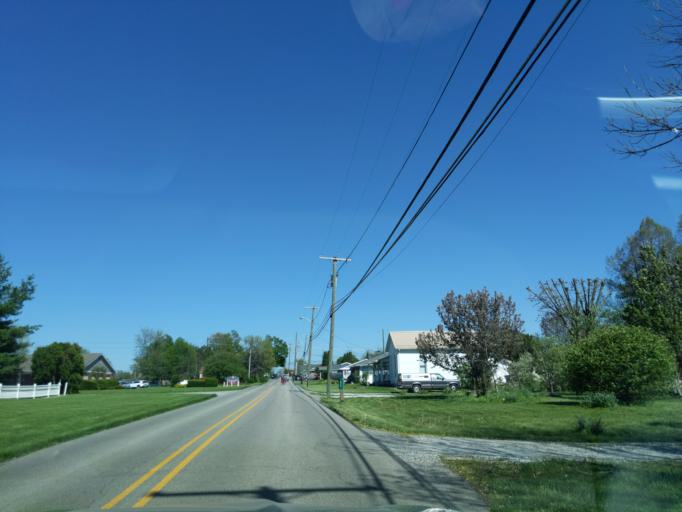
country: US
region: Indiana
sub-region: Decatur County
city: Greensburg
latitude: 39.3292
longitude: -85.4914
